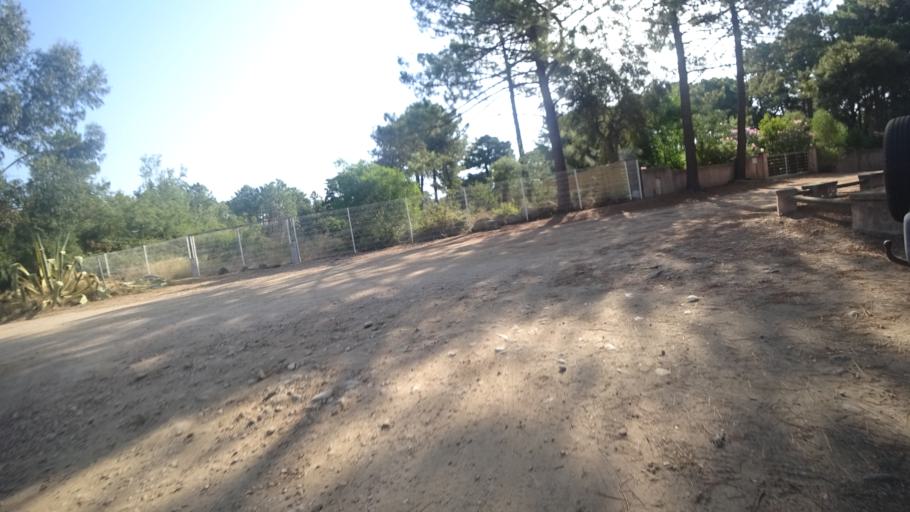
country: FR
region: Corsica
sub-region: Departement de la Corse-du-Sud
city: Porto-Vecchio
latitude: 41.6388
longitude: 9.3429
